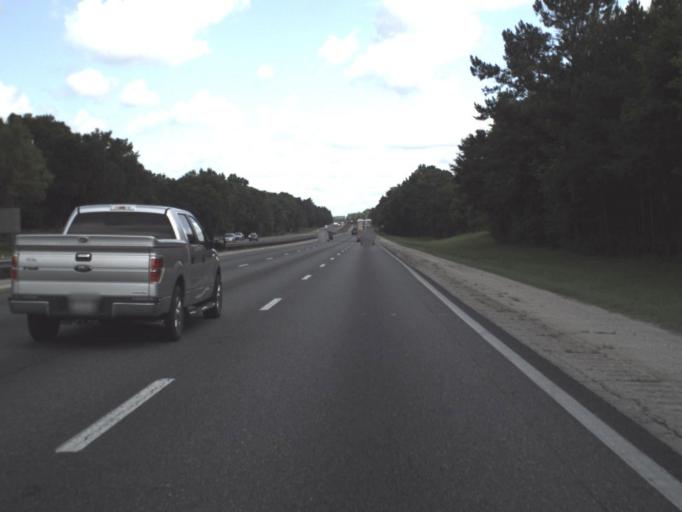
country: US
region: Florida
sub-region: Alachua County
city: Gainesville
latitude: 29.6287
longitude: -82.3939
